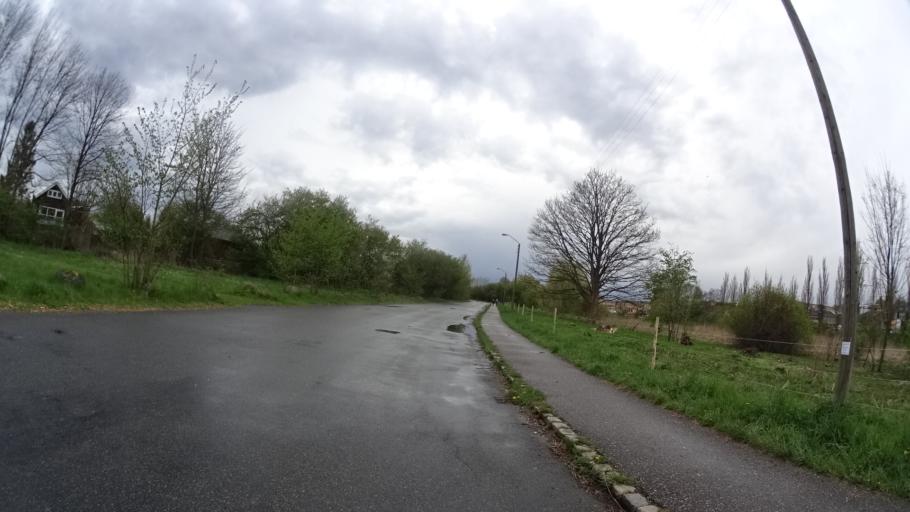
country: DK
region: Central Jutland
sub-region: Arhus Kommune
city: Arhus
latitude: 56.1530
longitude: 10.1818
